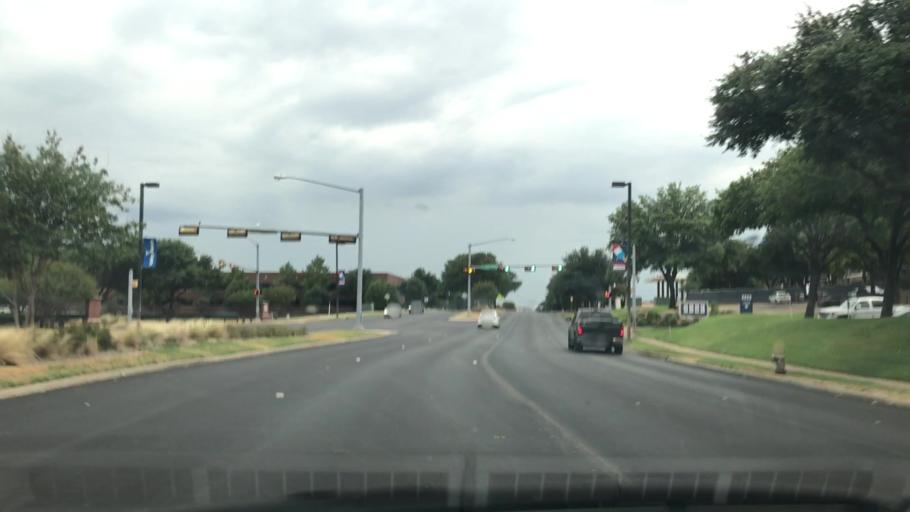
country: US
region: Texas
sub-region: Dallas County
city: Farmers Branch
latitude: 32.9442
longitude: -96.9521
